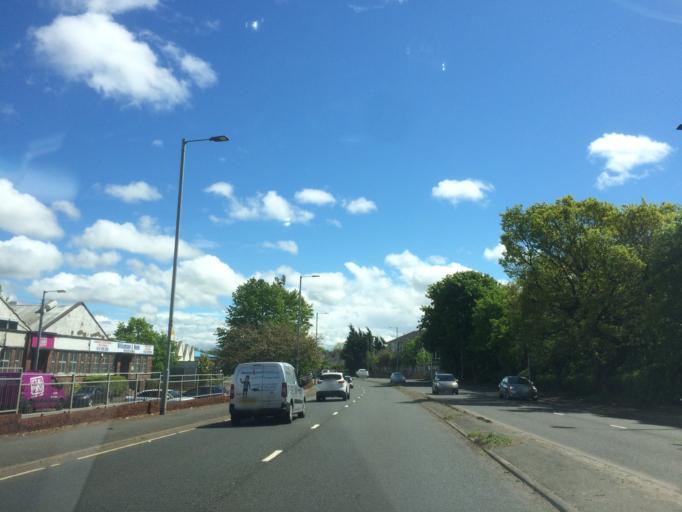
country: GB
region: Scotland
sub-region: East Renfrewshire
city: Newton Mearns
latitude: 55.8025
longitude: -4.3312
